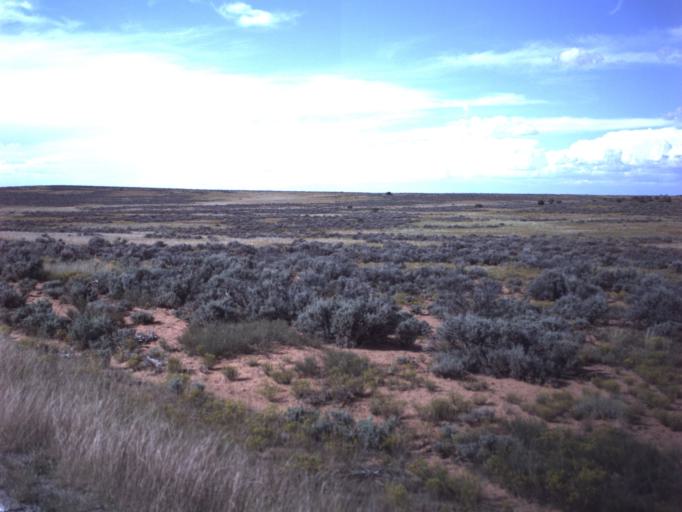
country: US
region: Utah
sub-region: Grand County
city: Moab
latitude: 38.5229
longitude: -109.7413
